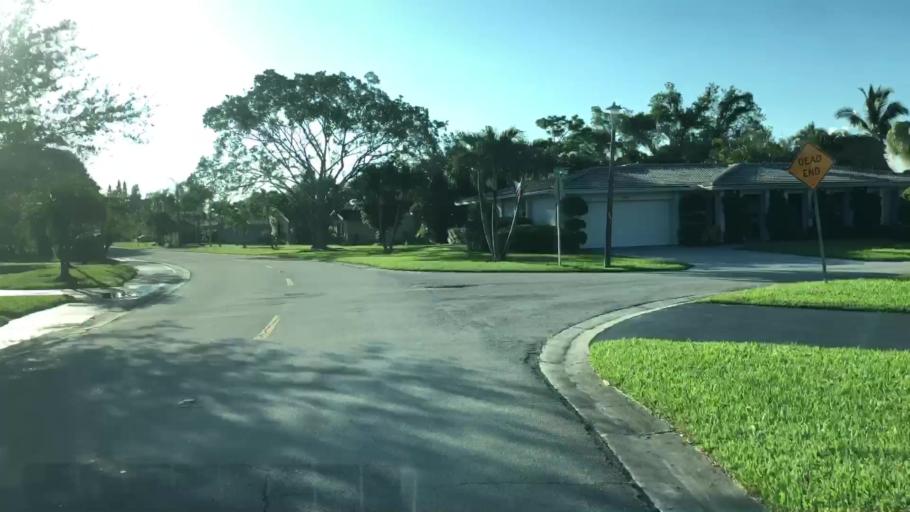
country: US
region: Florida
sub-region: Broward County
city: Coral Springs
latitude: 26.2775
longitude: -80.2641
